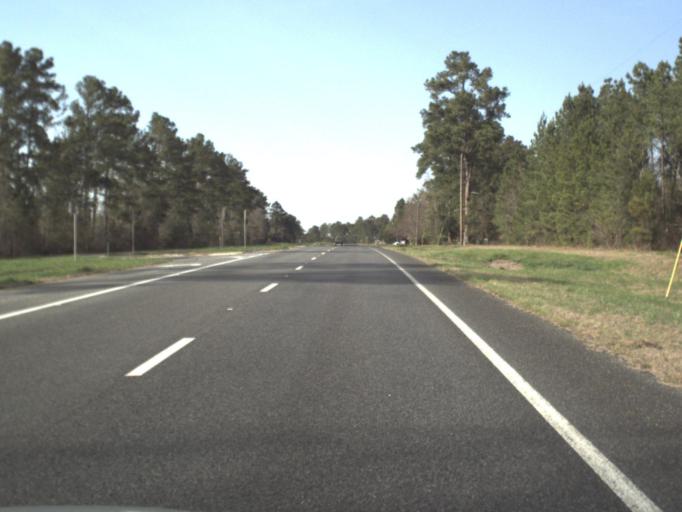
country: US
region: Florida
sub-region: Jefferson County
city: Monticello
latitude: 30.6580
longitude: -83.8774
